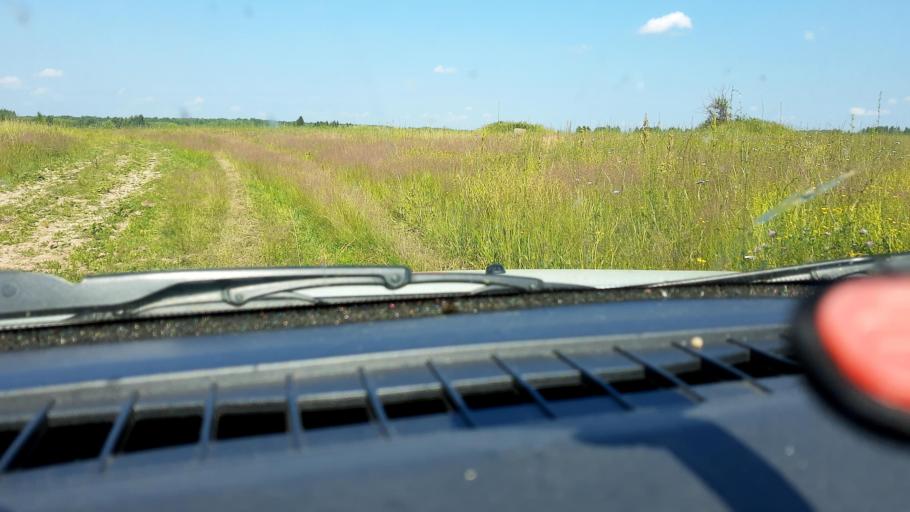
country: RU
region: Nizjnij Novgorod
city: Sharanga
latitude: 57.0466
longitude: 46.7222
